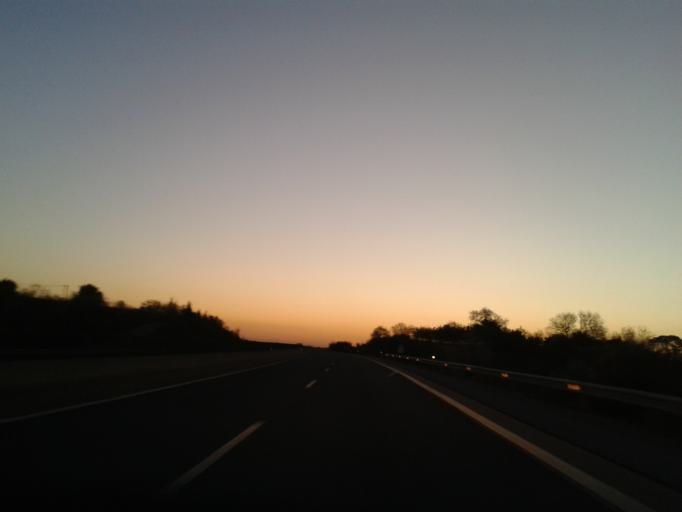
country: PT
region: Faro
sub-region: Albufeira
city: Guia
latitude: 37.1366
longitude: -8.2979
